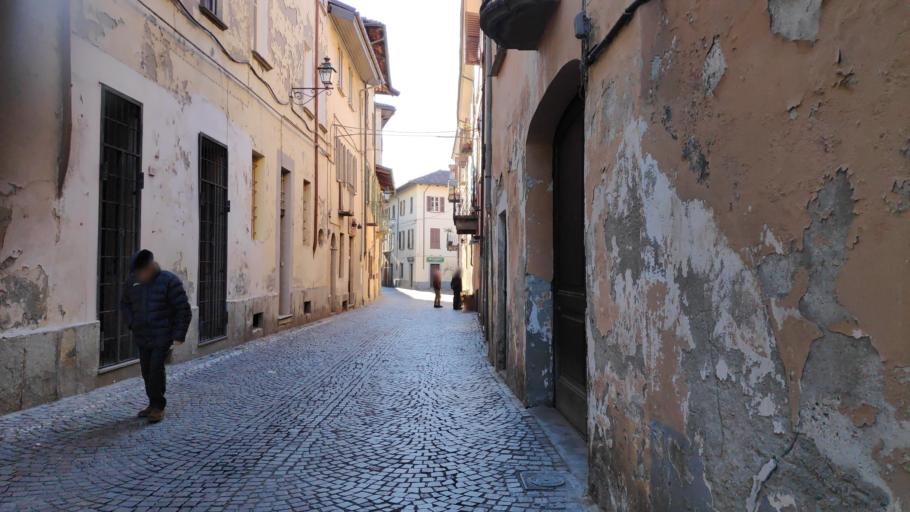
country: IT
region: Piedmont
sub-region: Provincia di Torino
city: Pinerolo
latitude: 44.8883
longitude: 7.3305
